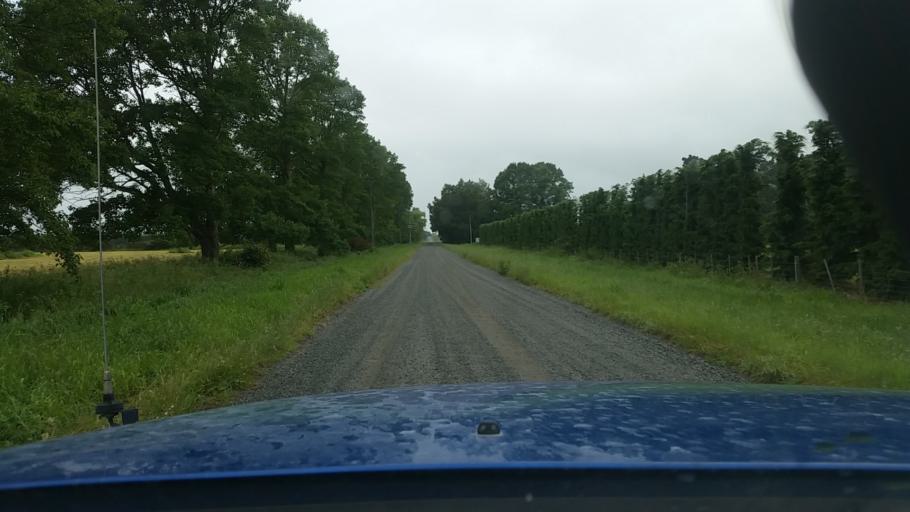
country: NZ
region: Canterbury
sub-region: Ashburton District
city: Tinwald
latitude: -43.9989
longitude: 171.6420
